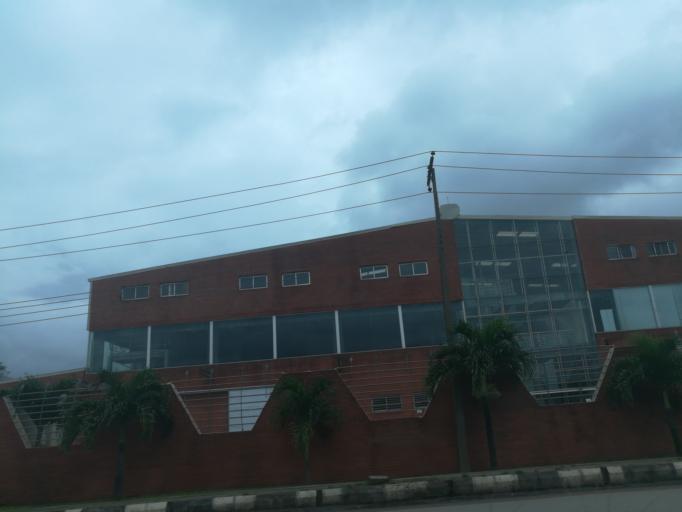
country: NG
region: Lagos
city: Agege
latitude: 6.6260
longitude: 3.3417
